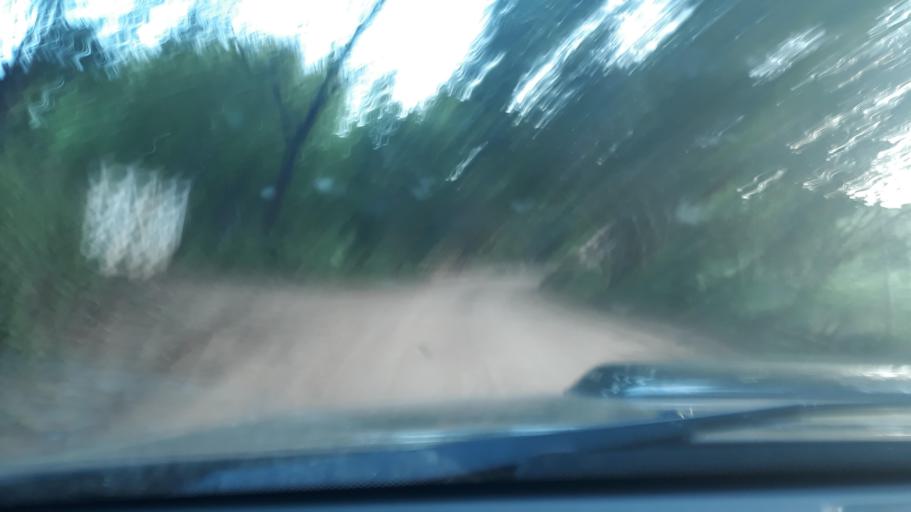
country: BR
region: Bahia
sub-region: Riacho De Santana
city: Riacho de Santana
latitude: -13.8126
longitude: -42.7209
